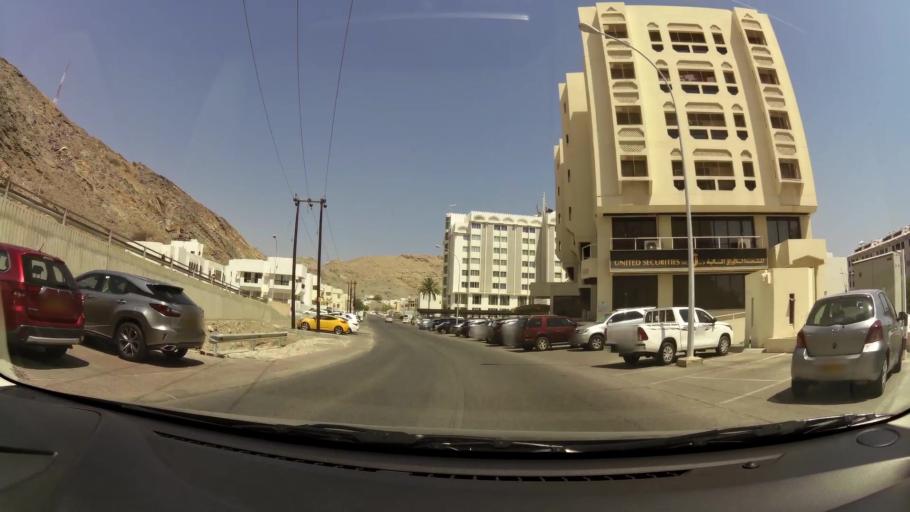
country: OM
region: Muhafazat Masqat
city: Muscat
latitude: 23.5953
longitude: 58.5409
